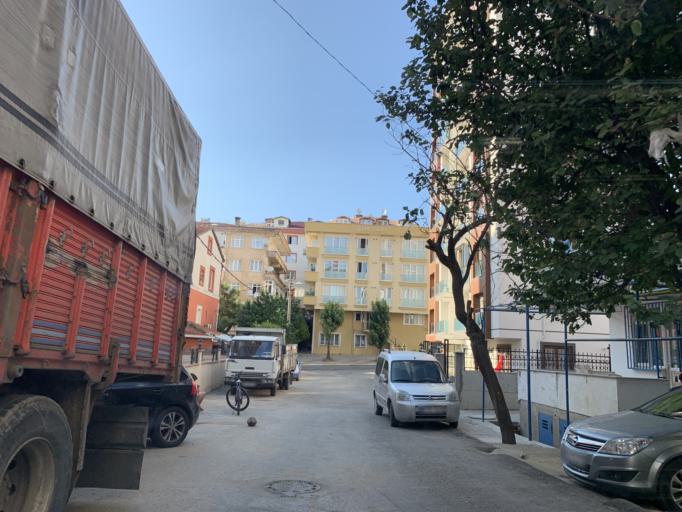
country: TR
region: Istanbul
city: Pendik
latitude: 40.8941
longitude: 29.2527
